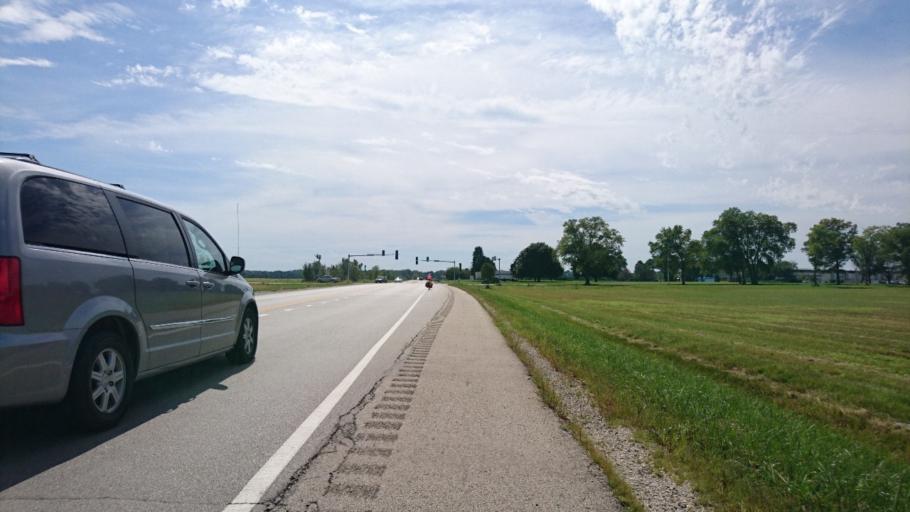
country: US
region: Illinois
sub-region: Will County
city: Wilmington
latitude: 41.3215
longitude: -88.1327
